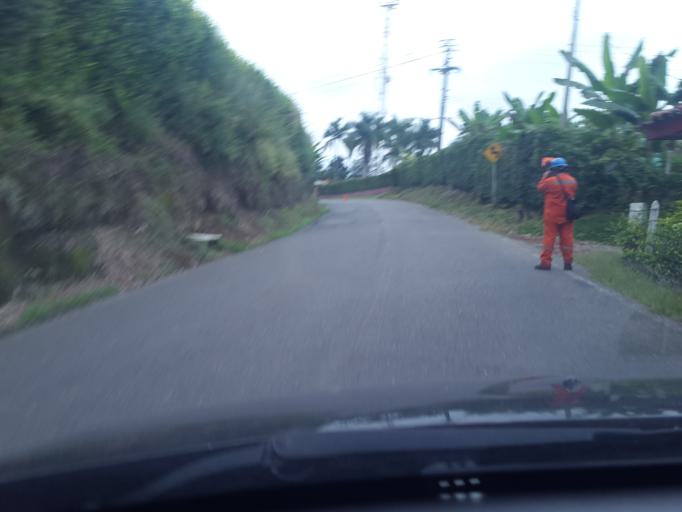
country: CO
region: Quindio
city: La Tebaida
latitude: 4.4855
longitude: -75.8036
